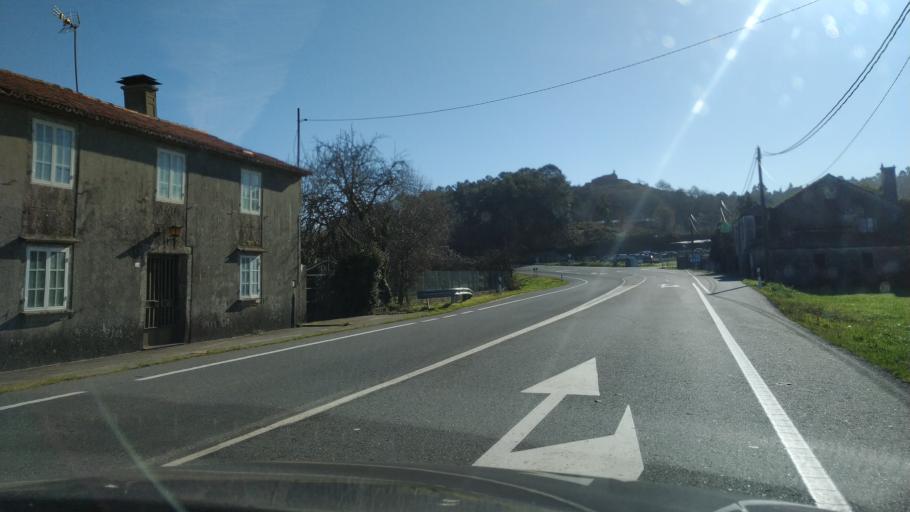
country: ES
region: Galicia
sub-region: Provincia da Coruna
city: Ribeira
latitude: 42.7490
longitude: -8.3472
